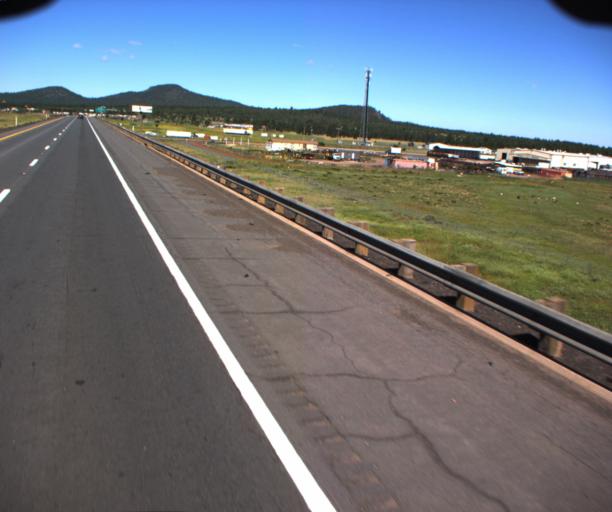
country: US
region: Arizona
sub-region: Coconino County
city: Williams
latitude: 35.2641
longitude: -112.1759
